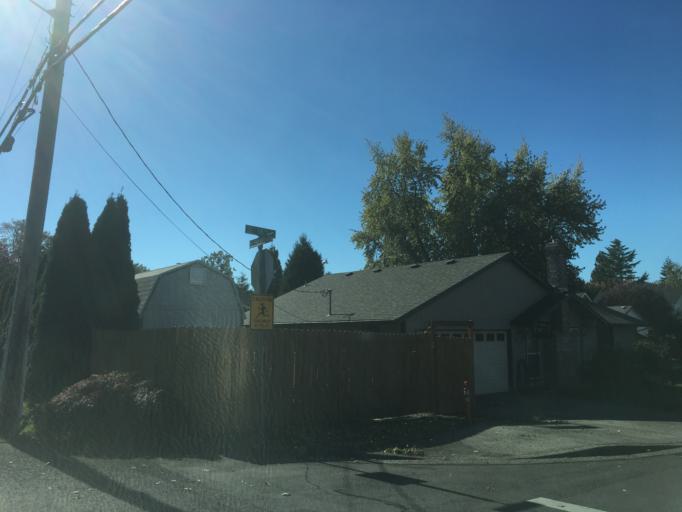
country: US
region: Oregon
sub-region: Multnomah County
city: Gresham
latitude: 45.4840
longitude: -122.4036
